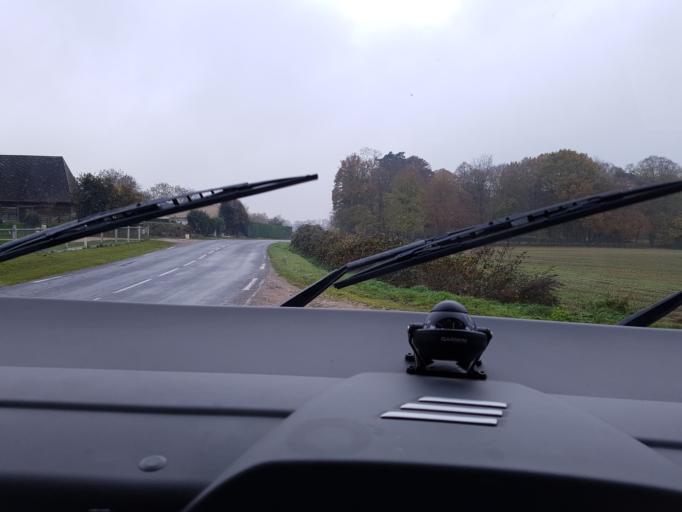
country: FR
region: Haute-Normandie
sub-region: Departement de l'Eure
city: Manneville-sur-Risle
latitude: 49.4076
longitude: 0.5385
